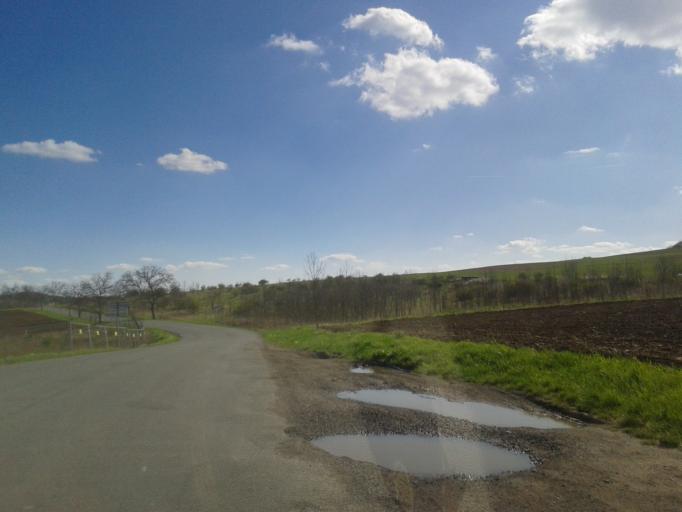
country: CZ
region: Central Bohemia
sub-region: Okres Beroun
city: Beroun
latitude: 49.9380
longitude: 14.0721
